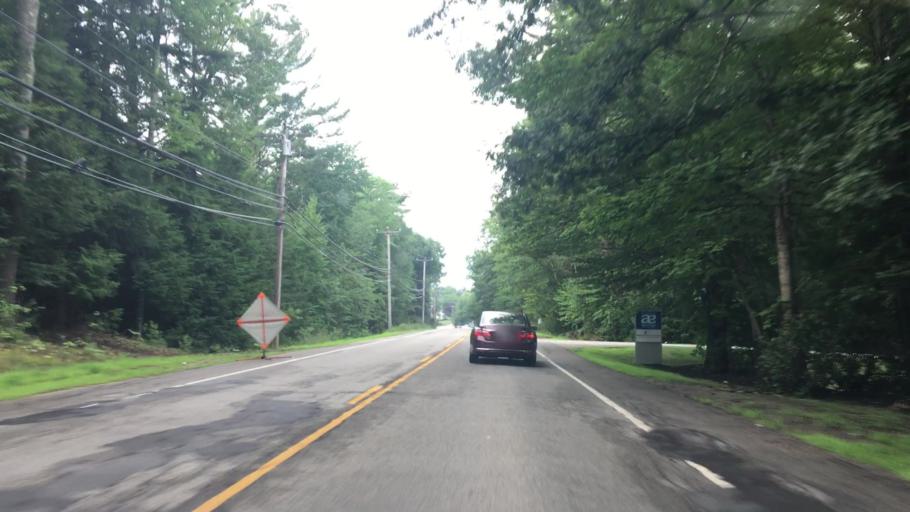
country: US
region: Maine
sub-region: York County
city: Sanford (historical)
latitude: 43.4547
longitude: -70.7653
